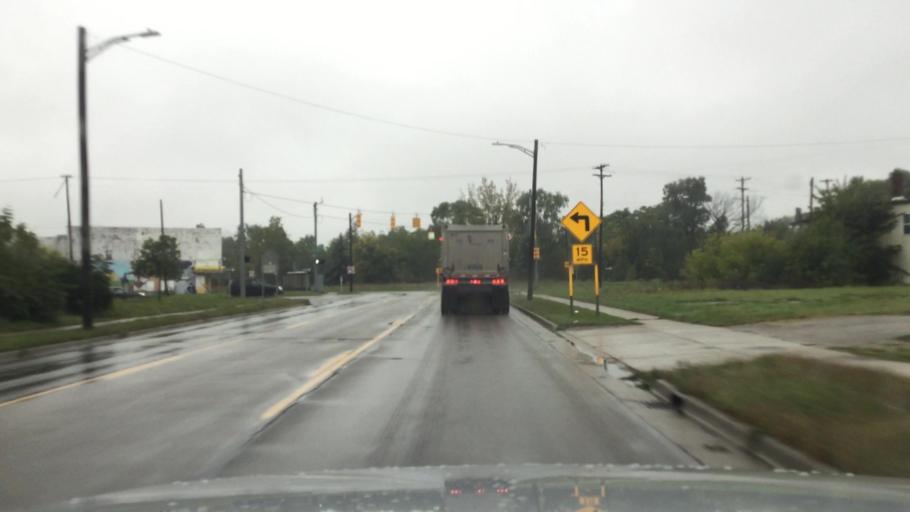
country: US
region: Michigan
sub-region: Saginaw County
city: Saginaw
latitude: 43.4031
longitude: -83.9588
